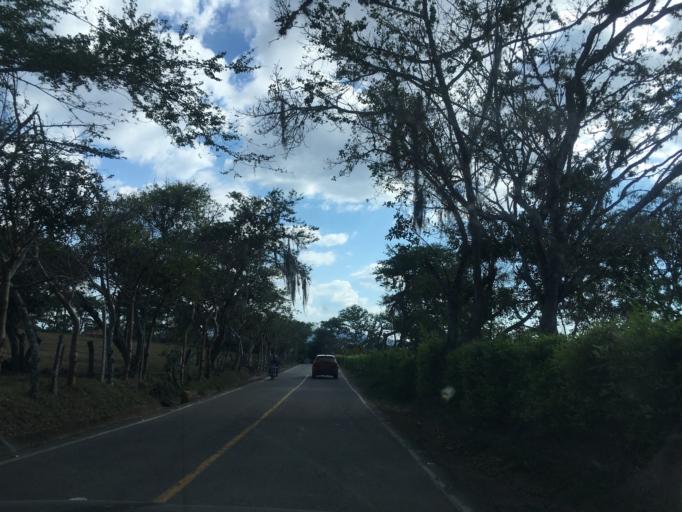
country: CO
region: Santander
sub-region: San Gil
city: San Gil
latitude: 6.5861
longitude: -73.1578
